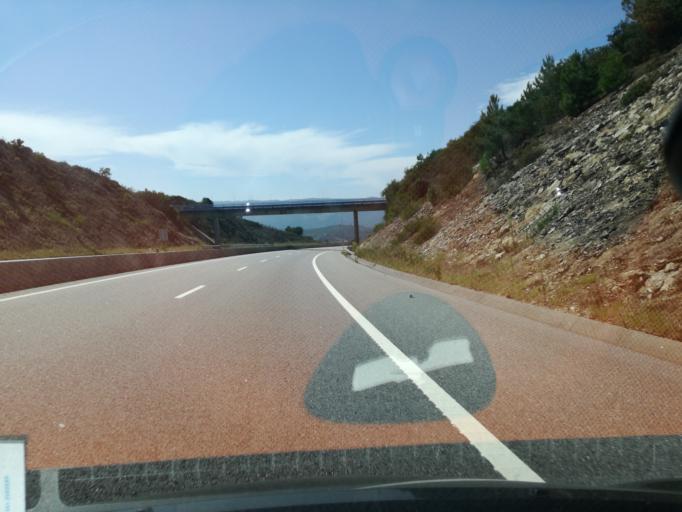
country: PT
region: Viana do Castelo
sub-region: Caminha
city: Vila Praia de Ancora
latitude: 41.8301
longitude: -8.7870
